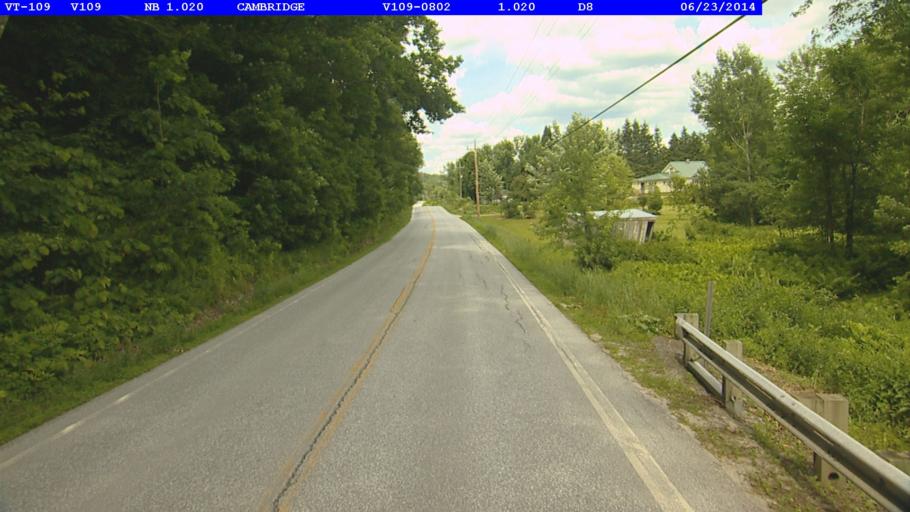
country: US
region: Vermont
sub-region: Lamoille County
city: Johnson
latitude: 44.6558
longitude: -72.8099
